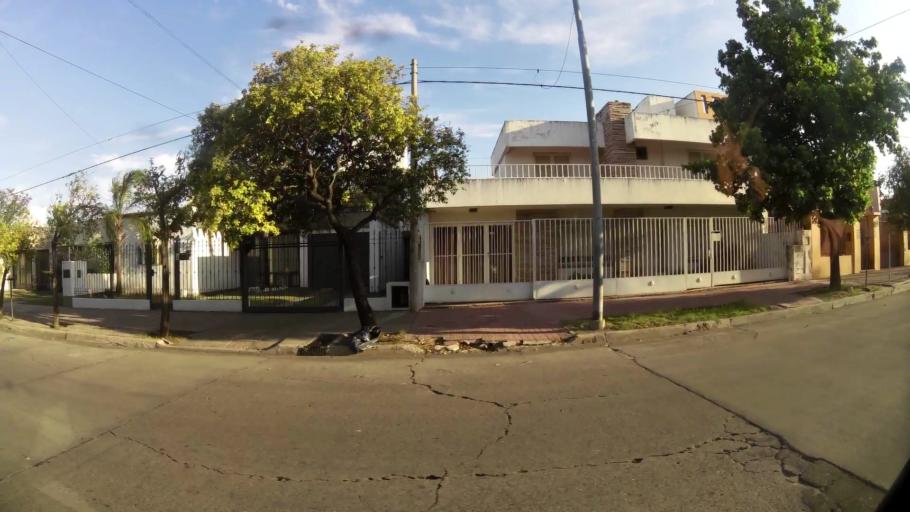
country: AR
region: Cordoba
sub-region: Departamento de Capital
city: Cordoba
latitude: -31.3864
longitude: -64.2304
